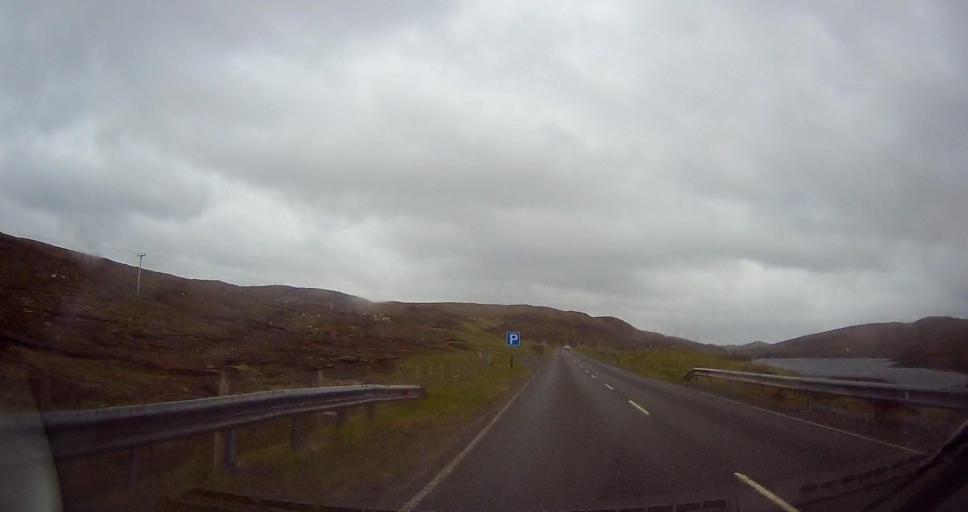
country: GB
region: Scotland
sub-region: Shetland Islands
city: Lerwick
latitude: 60.4463
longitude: -1.3963
